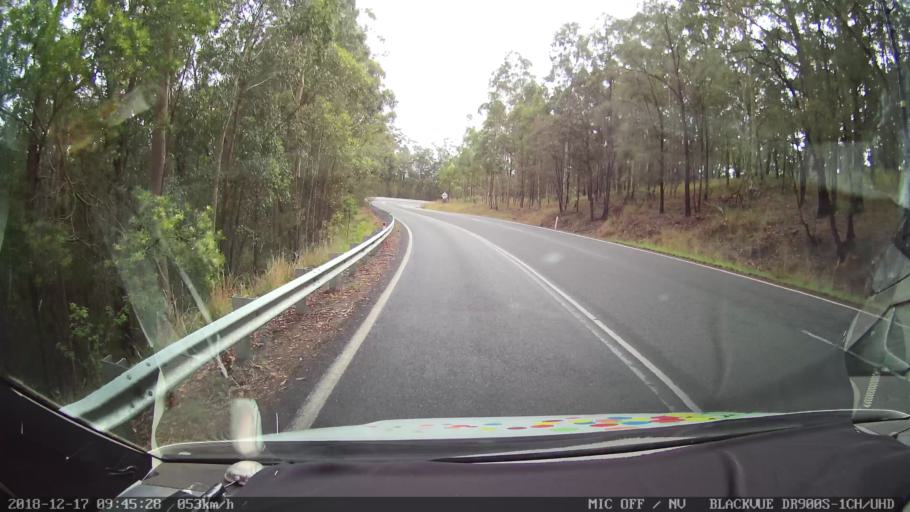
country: AU
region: New South Wales
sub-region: Tenterfield Municipality
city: Carrolls Creek
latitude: -28.9257
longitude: 152.3300
